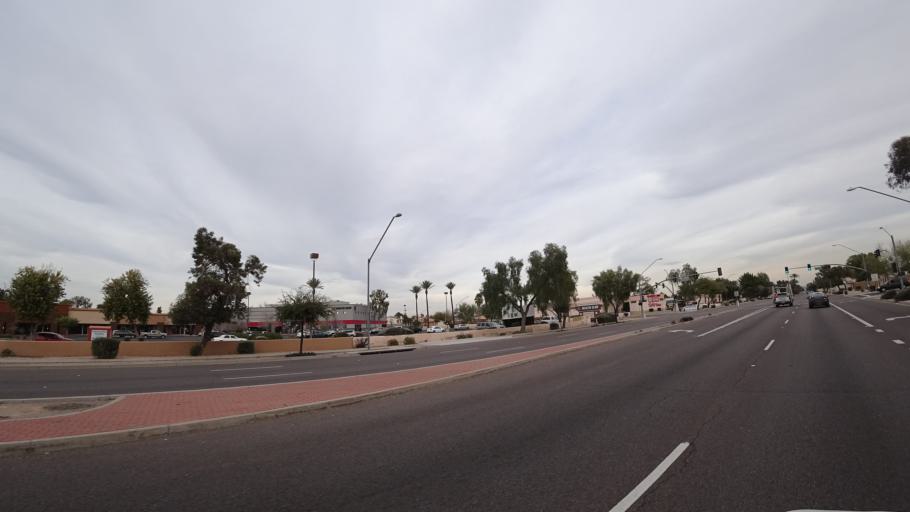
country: US
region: Arizona
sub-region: Maricopa County
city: Glendale
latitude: 33.5819
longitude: -112.1828
